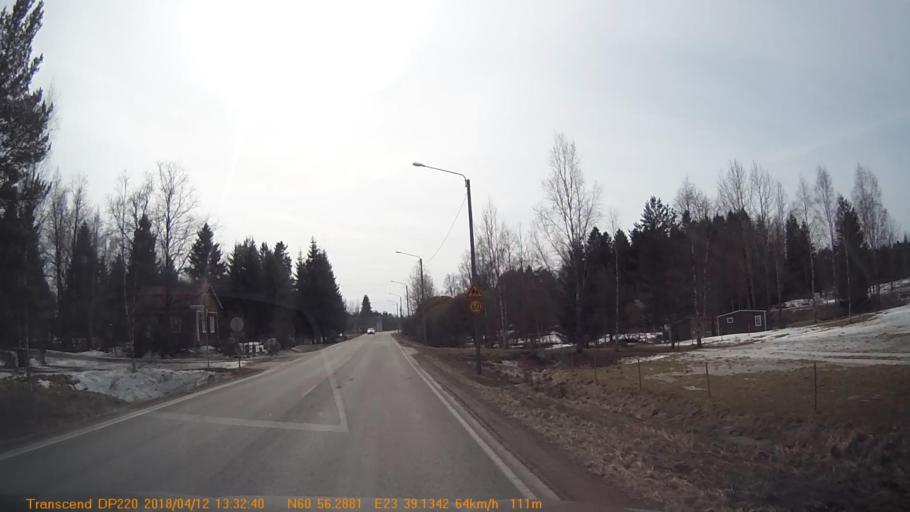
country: FI
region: Haeme
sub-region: Forssa
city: Forssa
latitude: 60.9380
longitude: 23.6521
